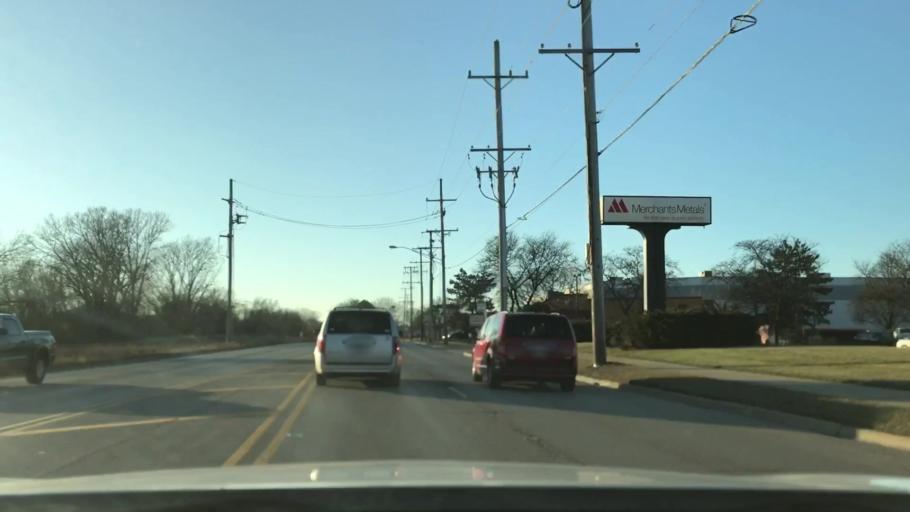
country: US
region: Illinois
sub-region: Kane County
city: Sleepy Hollow
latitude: 42.0584
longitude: -88.3169
